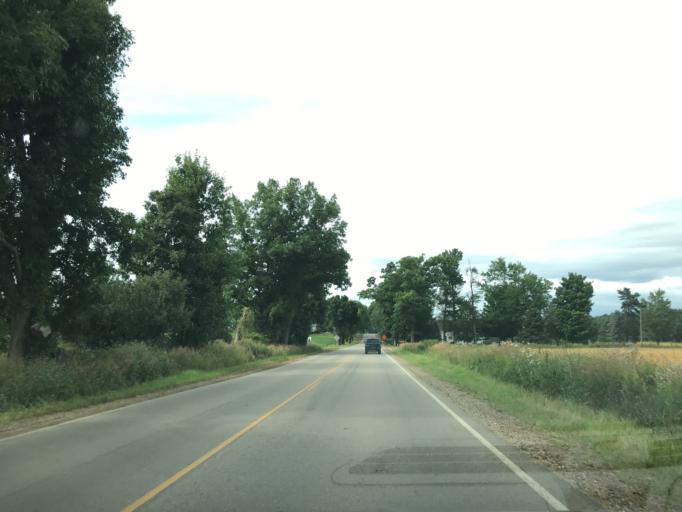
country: US
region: Michigan
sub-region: Jackson County
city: Spring Arbor
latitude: 42.0643
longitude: -84.5165
